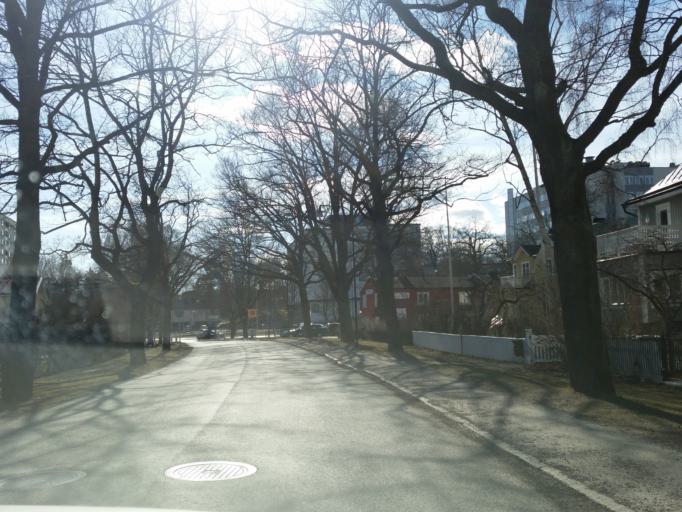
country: SE
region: Stockholm
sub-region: Sundbybergs Kommun
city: Sundbyberg
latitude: 59.3691
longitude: 17.9503
